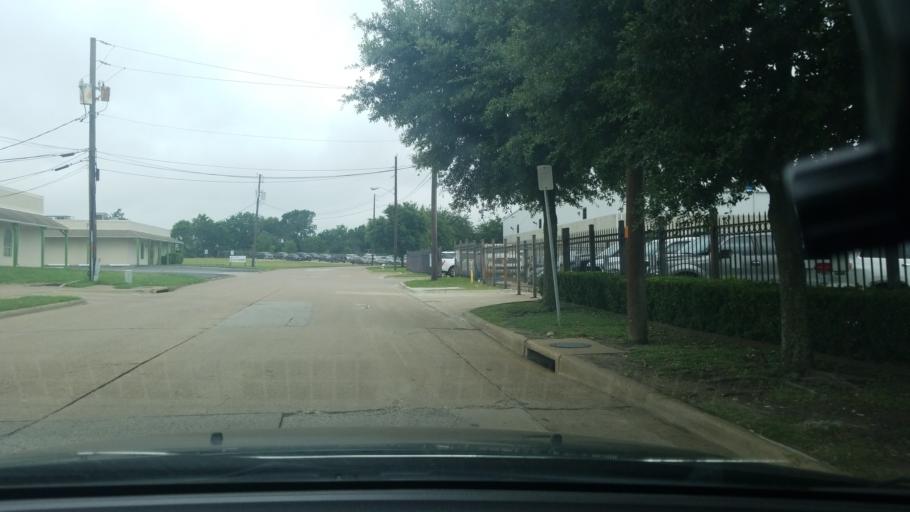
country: US
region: Texas
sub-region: Dallas County
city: Balch Springs
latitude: 32.7798
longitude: -96.6790
